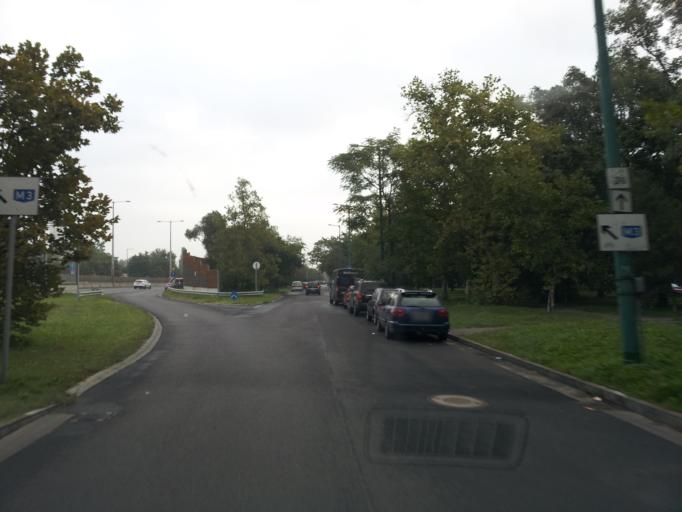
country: HU
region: Budapest
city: Budapest XIV. keruelet
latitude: 47.5345
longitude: 19.1035
